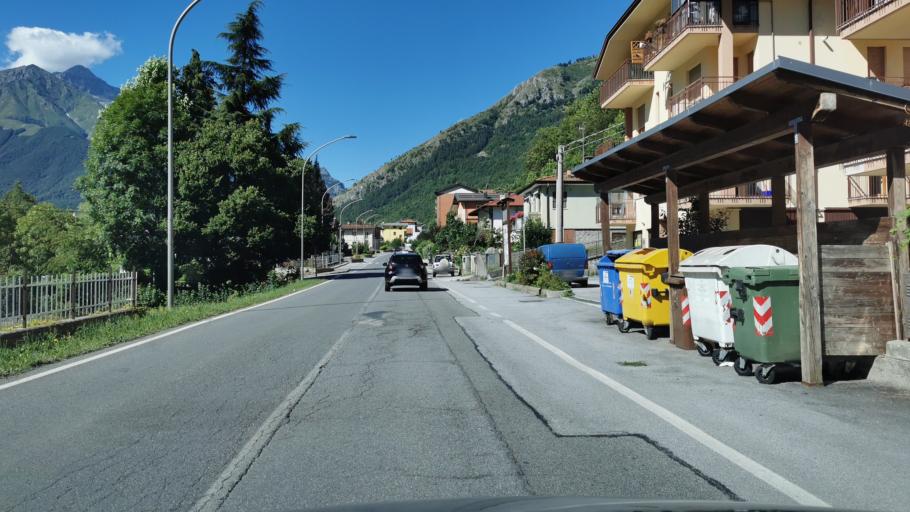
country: IT
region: Piedmont
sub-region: Provincia di Cuneo
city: Valdieri
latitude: 44.2788
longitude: 7.4025
